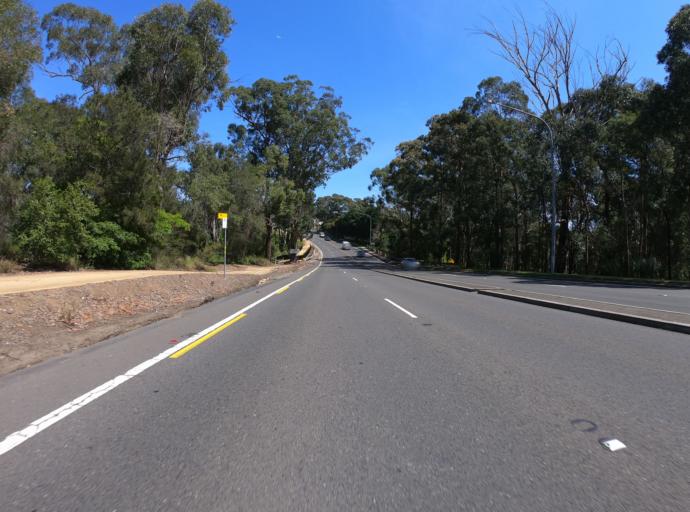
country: AU
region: New South Wales
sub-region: The Hills Shire
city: Castle Hill
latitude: -33.7234
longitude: 150.9831
